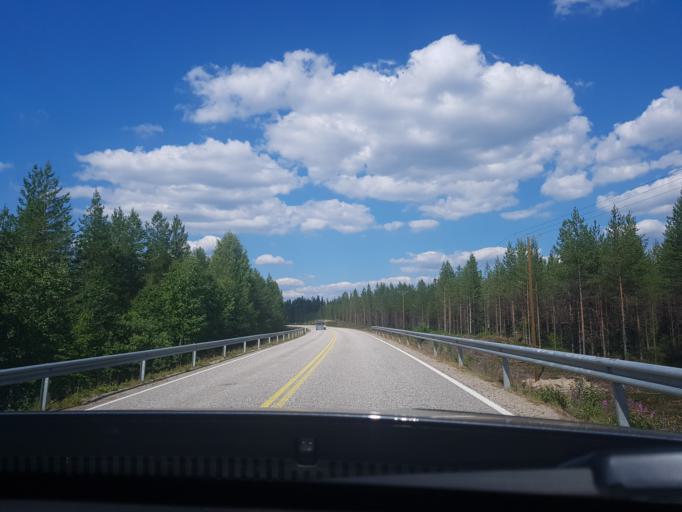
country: FI
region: Kainuu
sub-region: Kehys-Kainuu
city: Kuhmo
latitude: 64.2324
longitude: 29.8192
